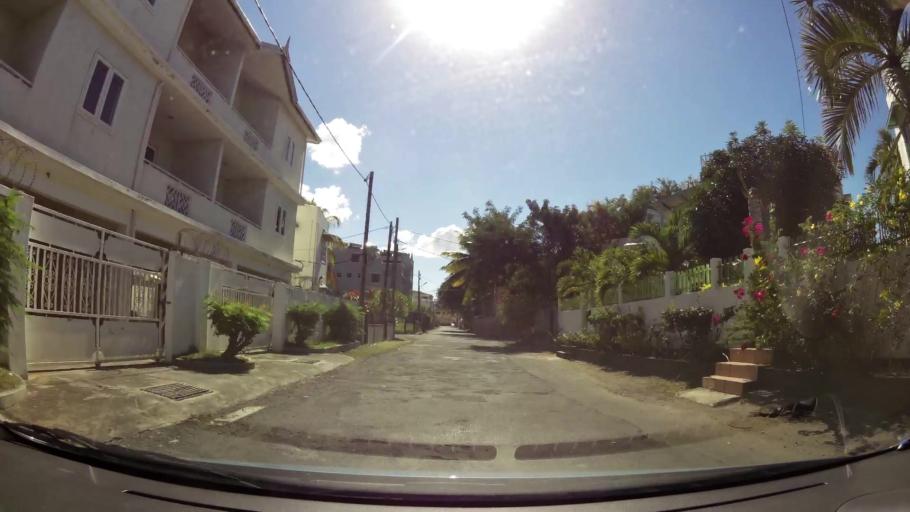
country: MU
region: Black River
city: Flic en Flac
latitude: -20.2870
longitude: 57.3647
